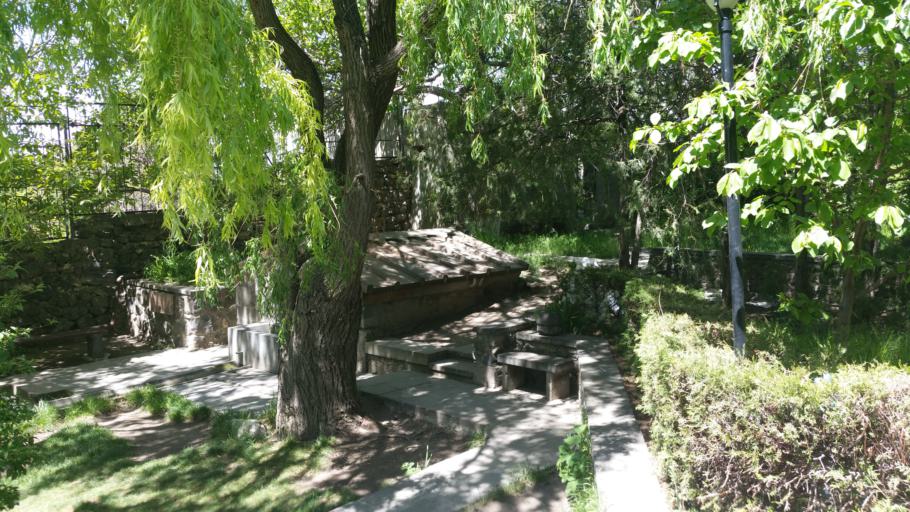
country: AM
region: Aragatsotn
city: Karbi
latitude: 40.3148
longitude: 44.3715
